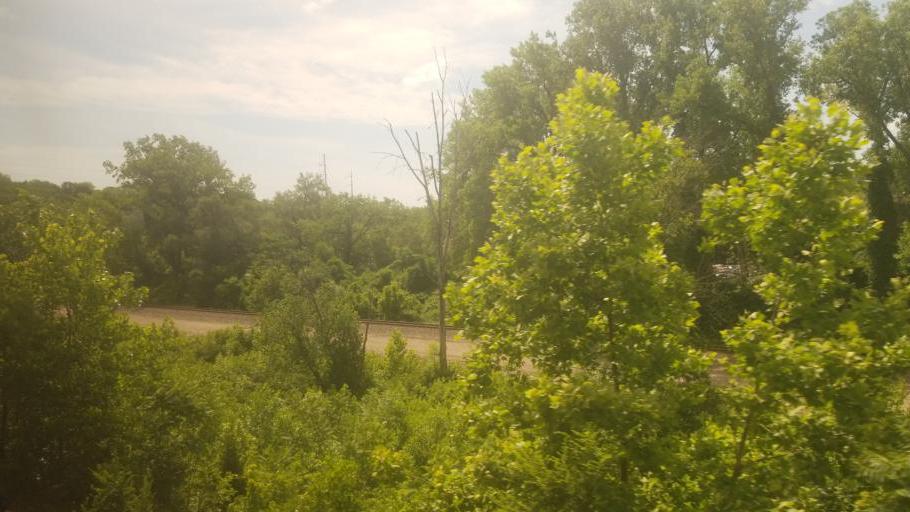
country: US
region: Missouri
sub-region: Jackson County
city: Sugar Creek
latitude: 39.1136
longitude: -94.4766
